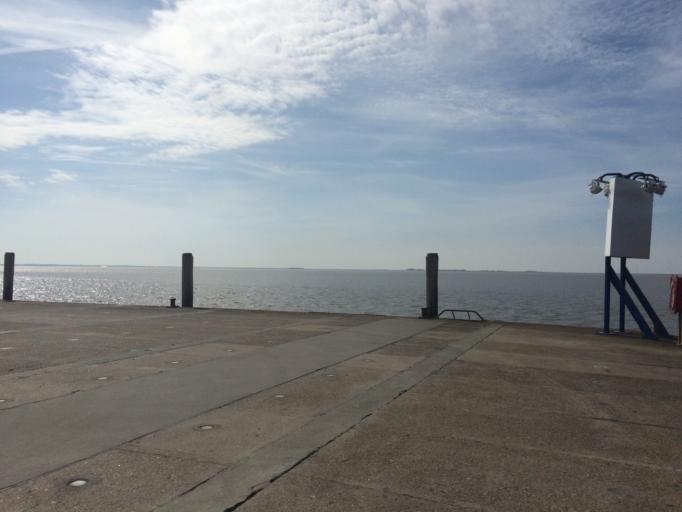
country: DE
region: Schleswig-Holstein
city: Dagebull
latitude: 54.7308
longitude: 8.6875
